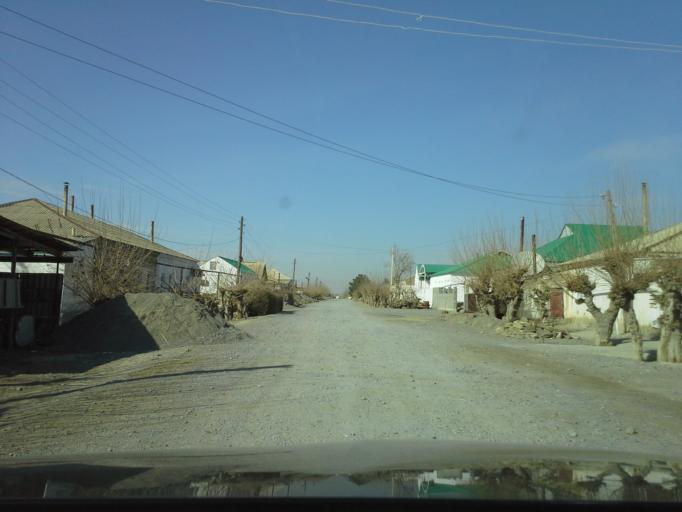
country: TM
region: Ahal
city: Abadan
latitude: 38.1222
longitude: 58.0002
